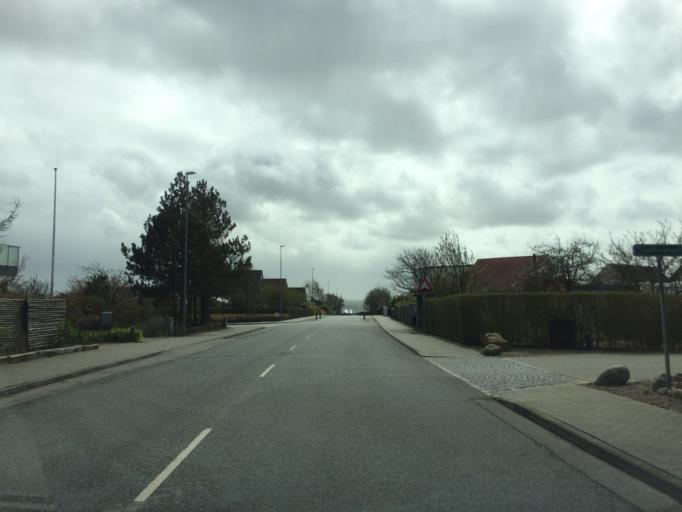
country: DK
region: South Denmark
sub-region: Fano Kommune
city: Nordby
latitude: 55.5310
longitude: 8.3484
